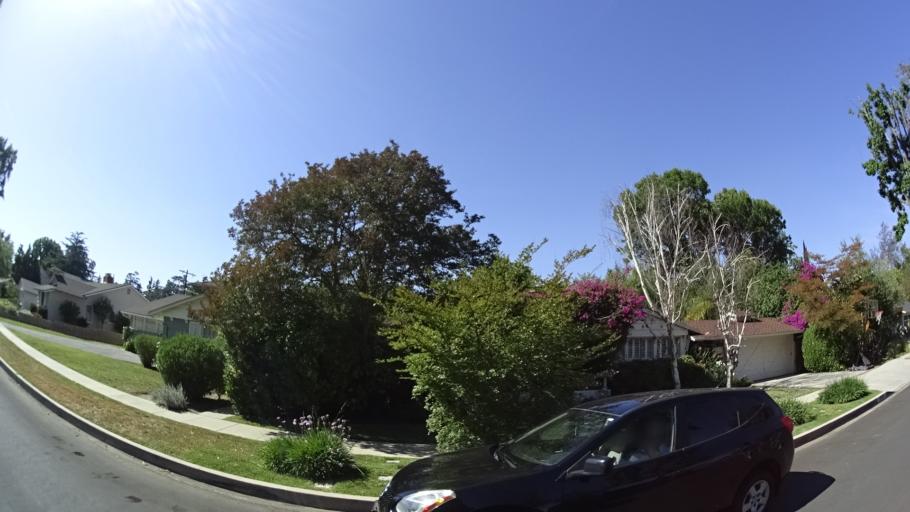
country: US
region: California
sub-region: Los Angeles County
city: Sherman Oaks
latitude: 34.1672
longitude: -118.4194
